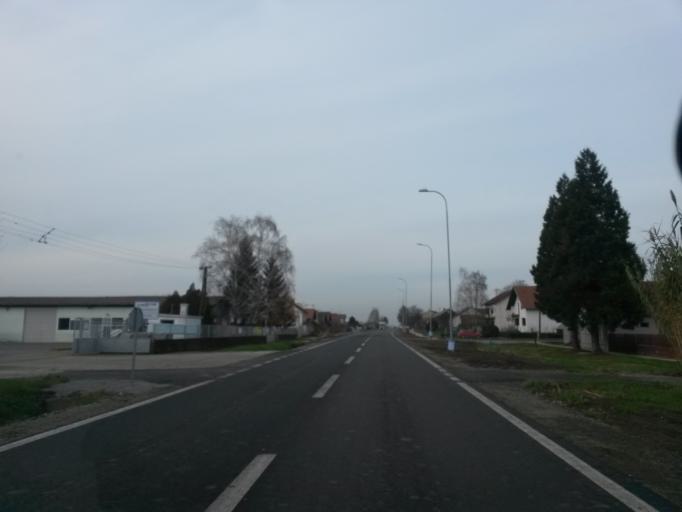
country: HR
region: Osjecko-Baranjska
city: Sarvas
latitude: 45.4778
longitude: 18.8301
